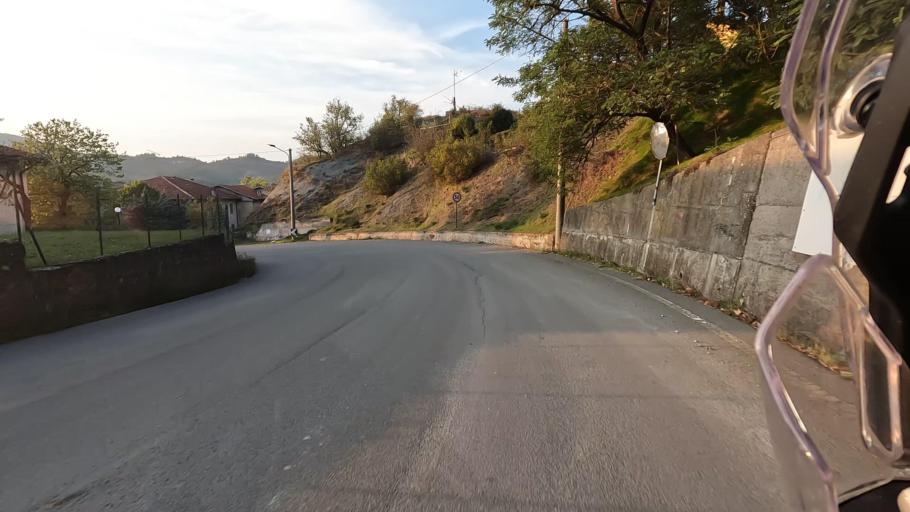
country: IT
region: Liguria
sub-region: Provincia di Savona
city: Mioglia
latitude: 44.4855
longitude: 8.4125
